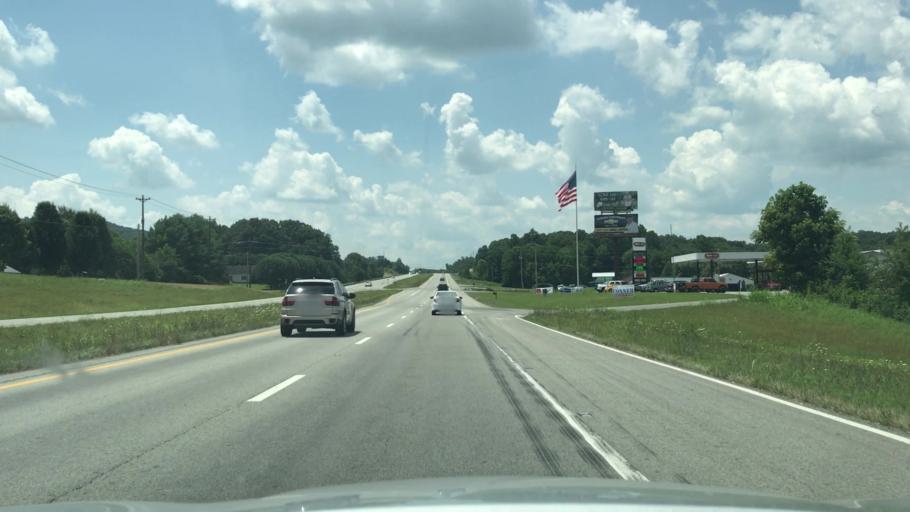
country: US
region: Tennessee
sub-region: Overton County
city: Livingston
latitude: 36.3329
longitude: -85.3543
